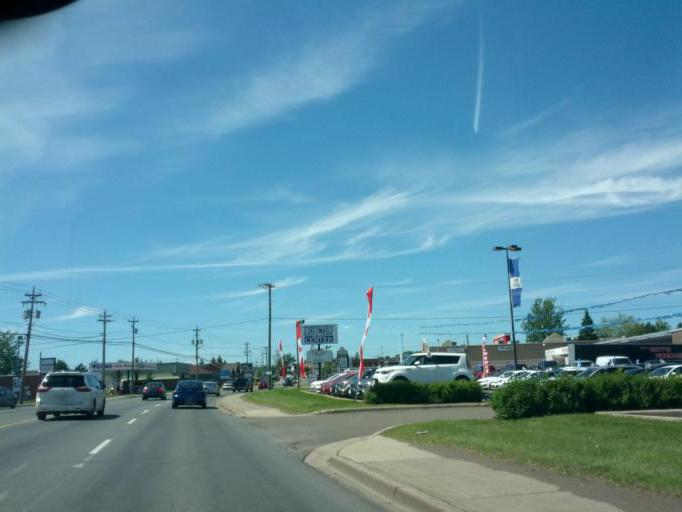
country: CA
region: New Brunswick
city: Moncton
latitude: 46.1150
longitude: -64.8381
